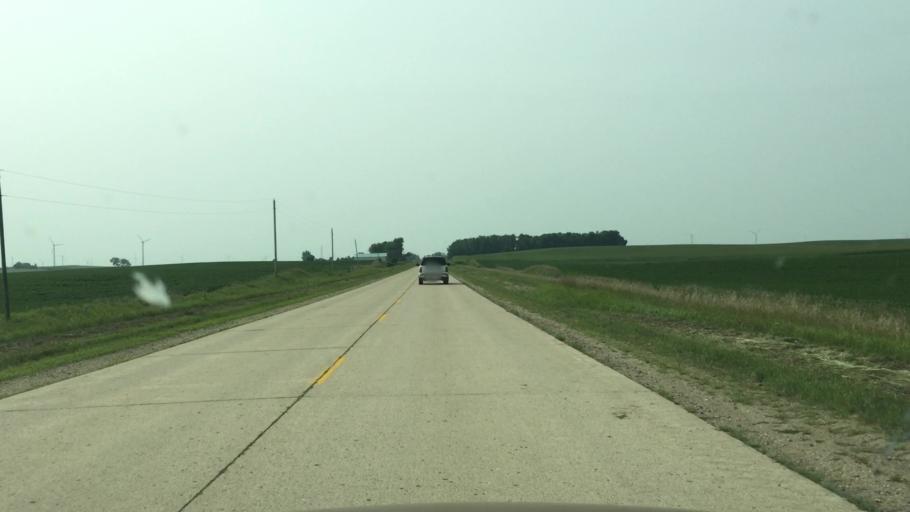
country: US
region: Iowa
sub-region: Dickinson County
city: Lake Park
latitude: 43.4269
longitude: -95.2891
